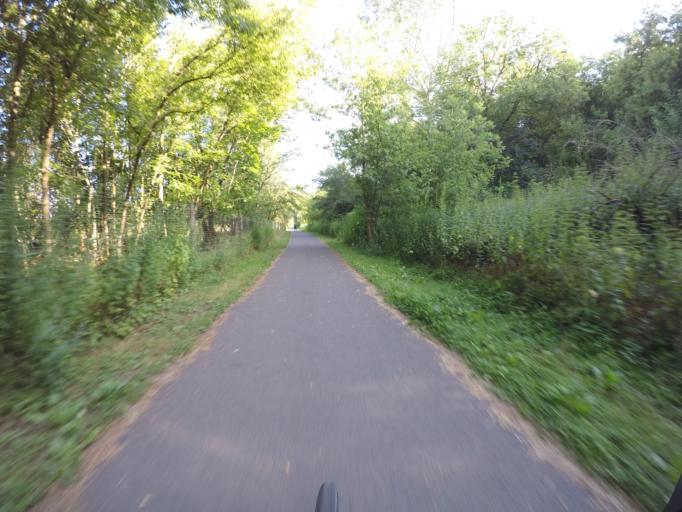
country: DE
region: Berlin
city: Stadtrandsiedlung Malchow
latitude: 52.5766
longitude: 13.4921
